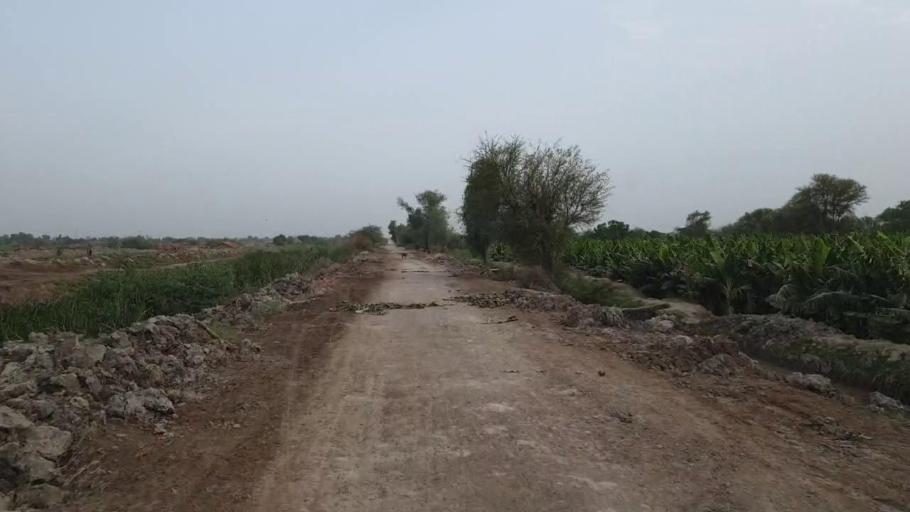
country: PK
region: Sindh
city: Daur
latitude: 26.4267
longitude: 68.2251
